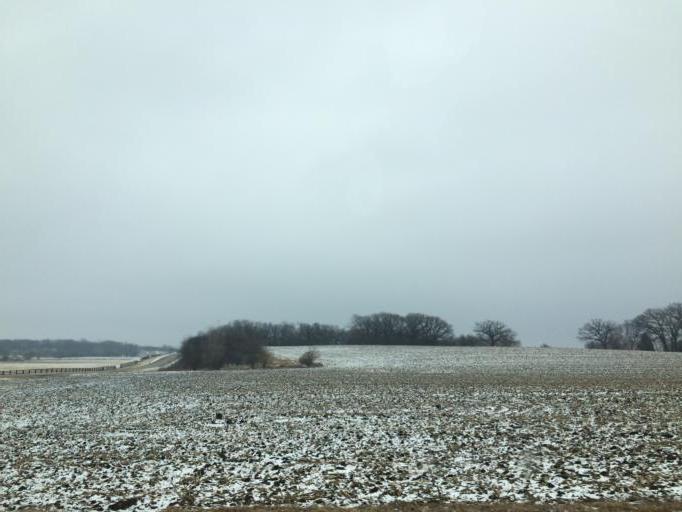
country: US
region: Illinois
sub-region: McHenry County
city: Huntley
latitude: 42.2146
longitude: -88.4224
